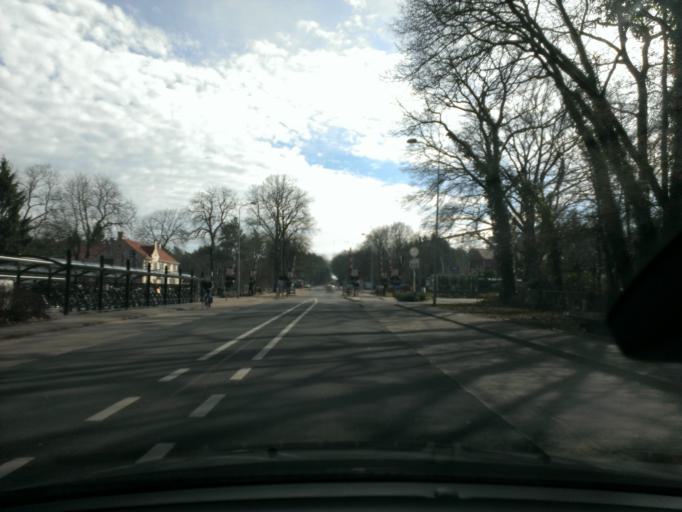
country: NL
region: Gelderland
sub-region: Gemeente Hattem
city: Hattem
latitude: 52.4546
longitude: 6.0020
